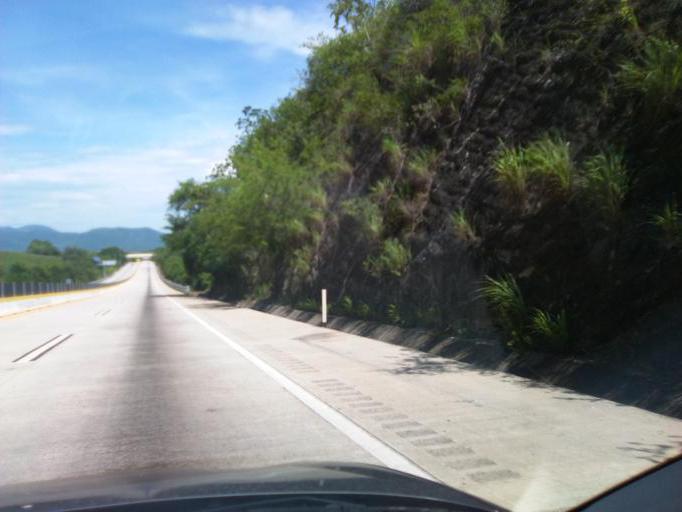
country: MX
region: Guerrero
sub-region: Acapulco de Juarez
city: Kilometro 30
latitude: 16.9663
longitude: -99.7329
